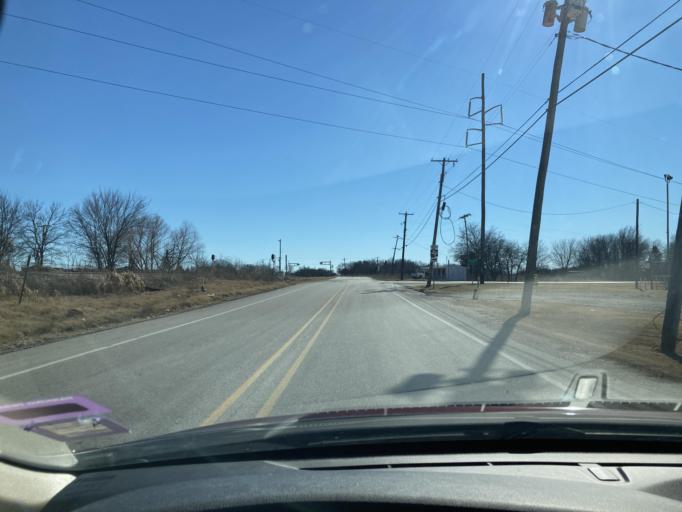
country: US
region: Texas
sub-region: Navarro County
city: Corsicana
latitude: 32.0703
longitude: -96.4636
